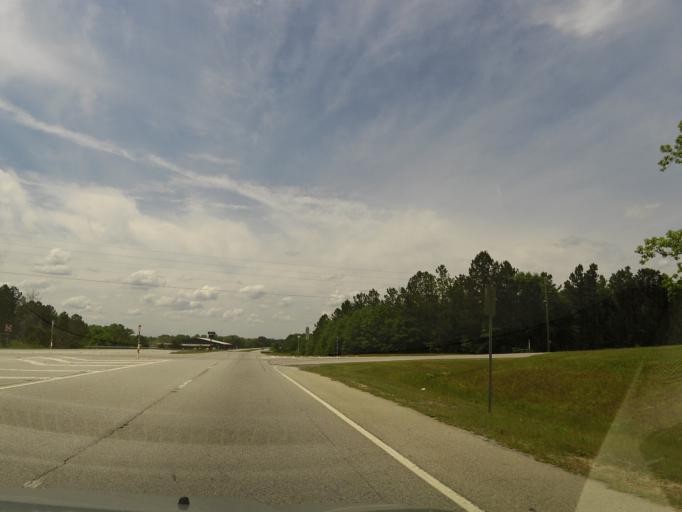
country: US
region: Georgia
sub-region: Emanuel County
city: Swainsboro
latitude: 32.5689
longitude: -82.3485
